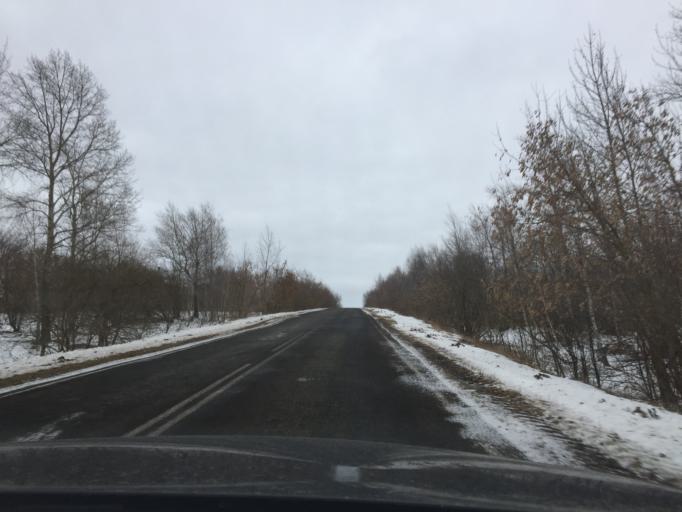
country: RU
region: Tula
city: Shchekino
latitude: 53.8217
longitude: 37.5246
